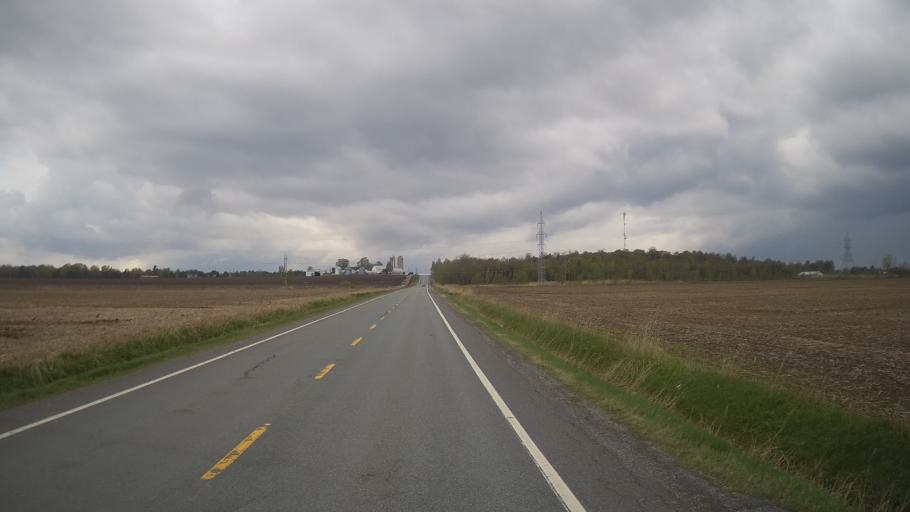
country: CA
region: Quebec
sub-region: Monteregie
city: Farnham
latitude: 45.2628
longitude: -72.9311
